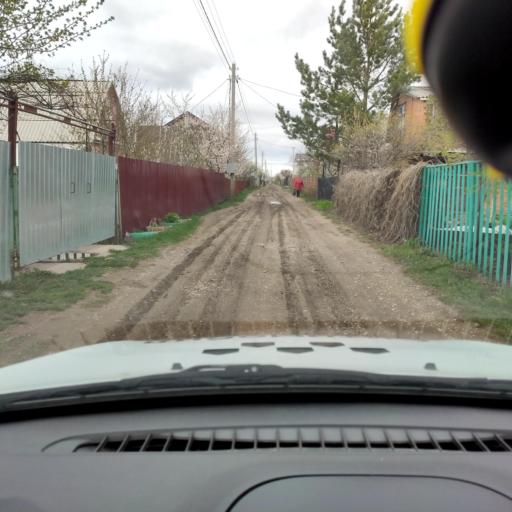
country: RU
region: Samara
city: Tol'yatti
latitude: 53.5820
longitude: 49.3157
